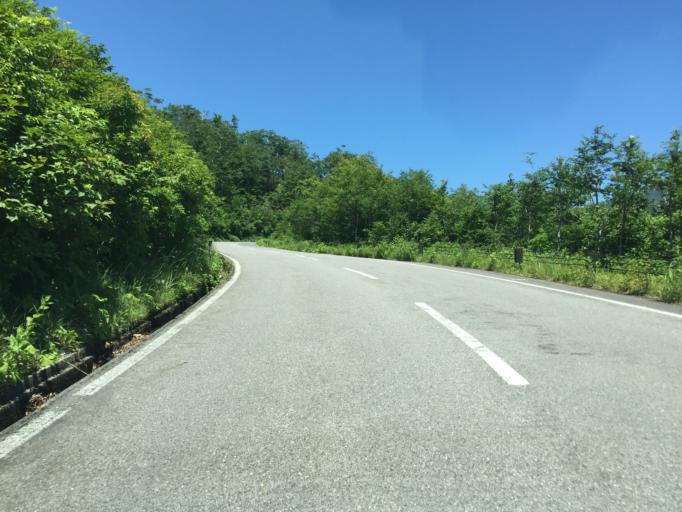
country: JP
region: Fukushima
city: Inawashiro
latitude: 37.6786
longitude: 140.2323
